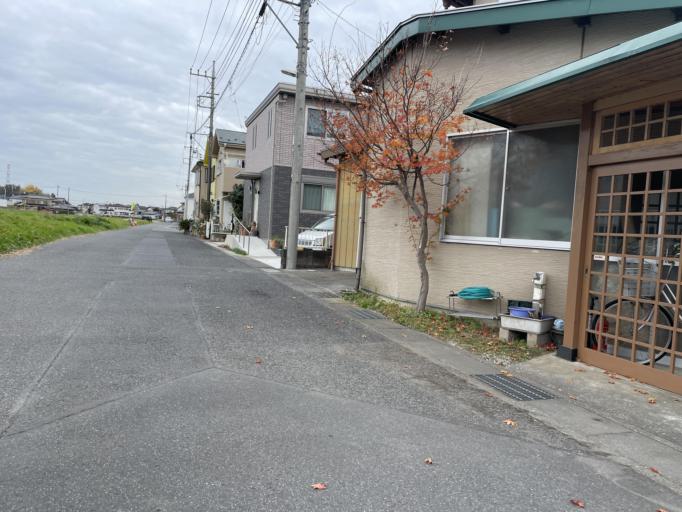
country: JP
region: Saitama
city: Shiraoka
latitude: 36.0296
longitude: 139.6520
